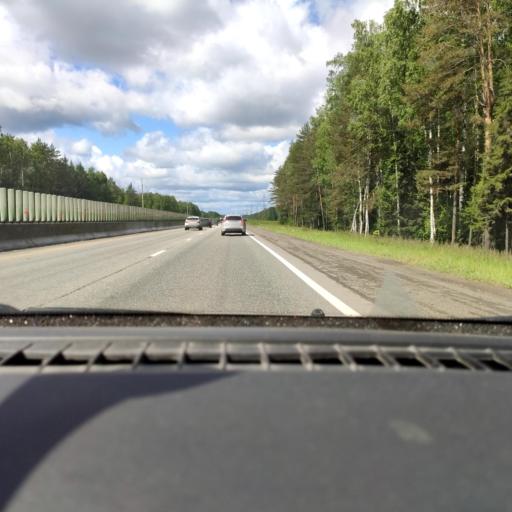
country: RU
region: Perm
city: Overyata
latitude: 58.0374
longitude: 55.9638
